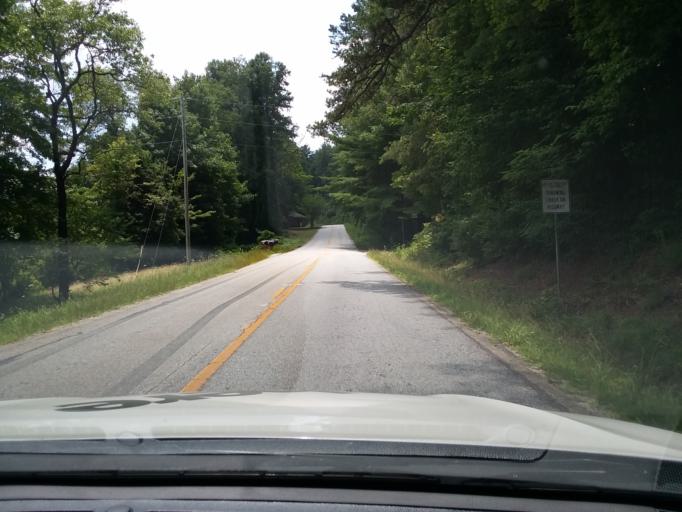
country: US
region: Georgia
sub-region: Rabun County
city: Mountain City
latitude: 34.9960
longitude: -83.1962
